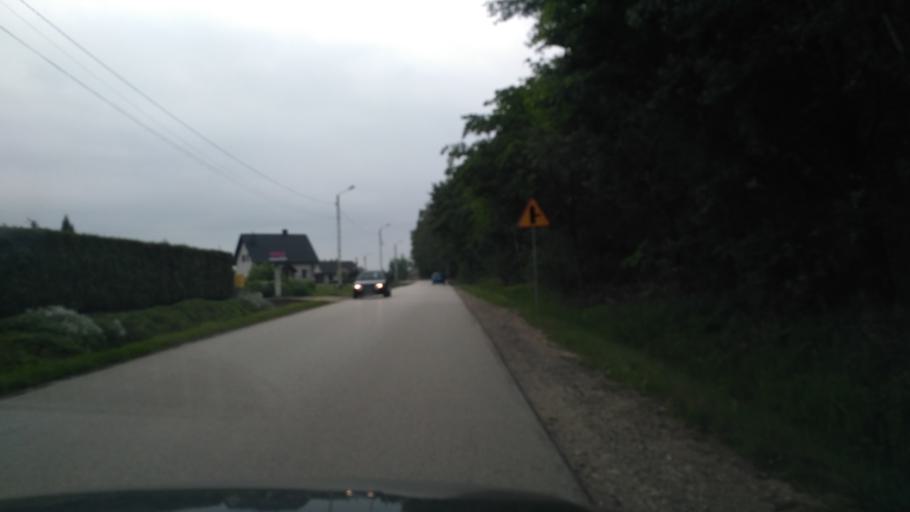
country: PL
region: Subcarpathian Voivodeship
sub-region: Powiat ropczycko-sedziszowski
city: Sedziszow Malopolski
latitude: 50.1136
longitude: 21.6739
